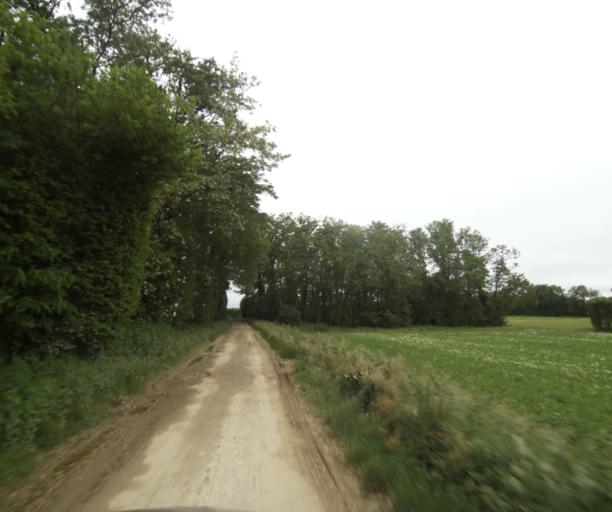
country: FR
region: Rhone-Alpes
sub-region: Departement de l'Ain
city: Miribel
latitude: 45.8464
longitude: 4.9241
